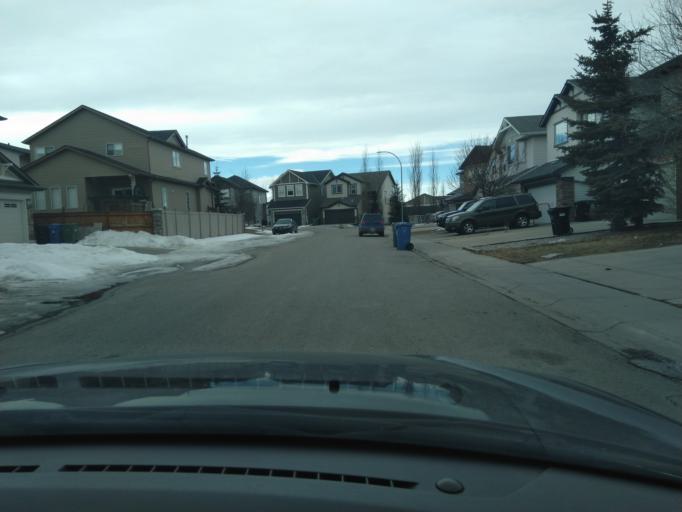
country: CA
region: Alberta
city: Calgary
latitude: 51.1590
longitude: -114.0891
